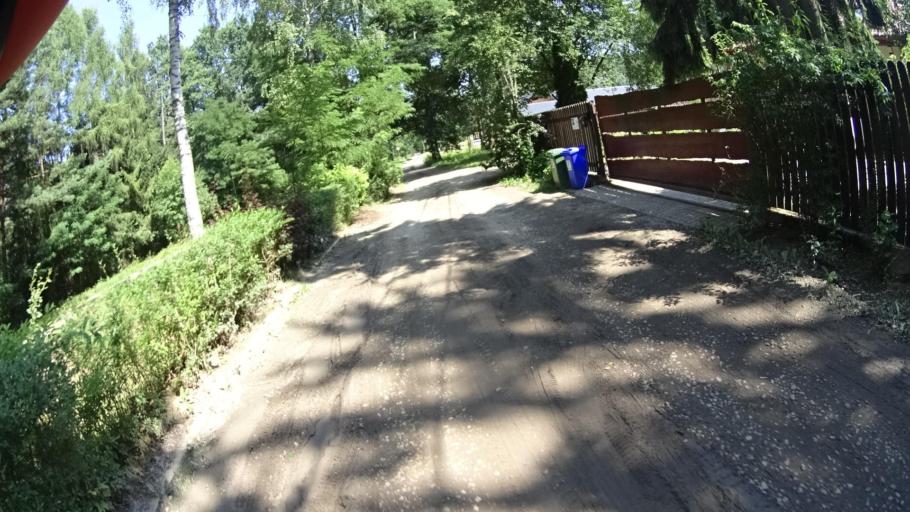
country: PL
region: Masovian Voivodeship
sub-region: Powiat piaseczynski
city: Prazmow
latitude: 52.0085
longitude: 20.9175
